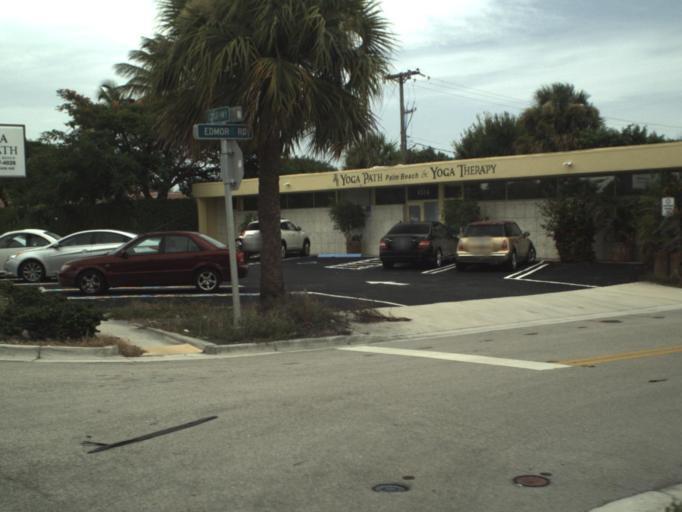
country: US
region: Florida
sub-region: Palm Beach County
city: Lake Clarke Shores
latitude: 26.6716
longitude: -80.0550
